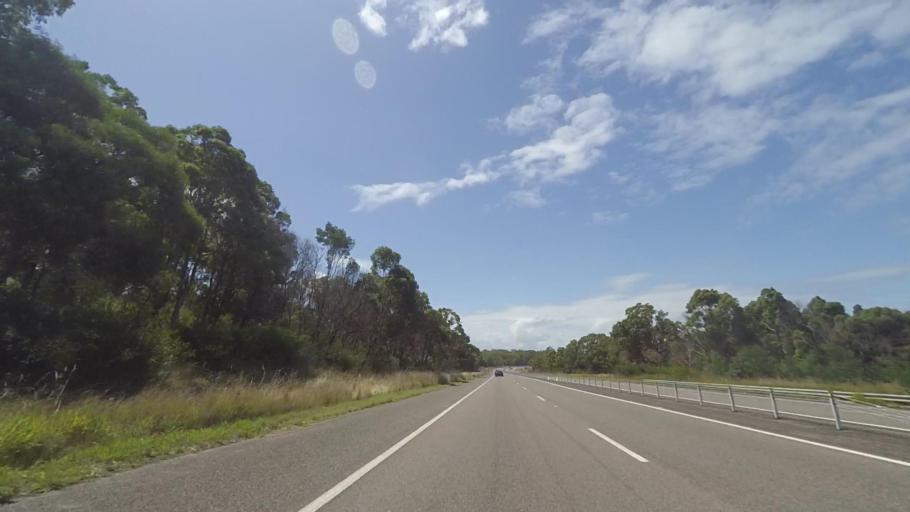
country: AU
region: New South Wales
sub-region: Wyong Shire
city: Kingfisher Shores
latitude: -33.1421
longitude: 151.6100
